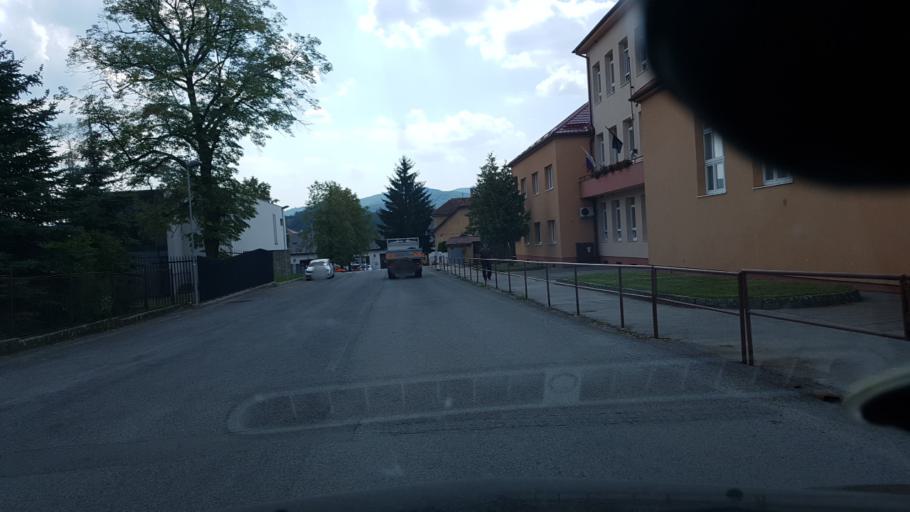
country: SK
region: Banskobystricky
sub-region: Okres Banska Bystrica
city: Zvolen
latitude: 48.5620
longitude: 19.2584
